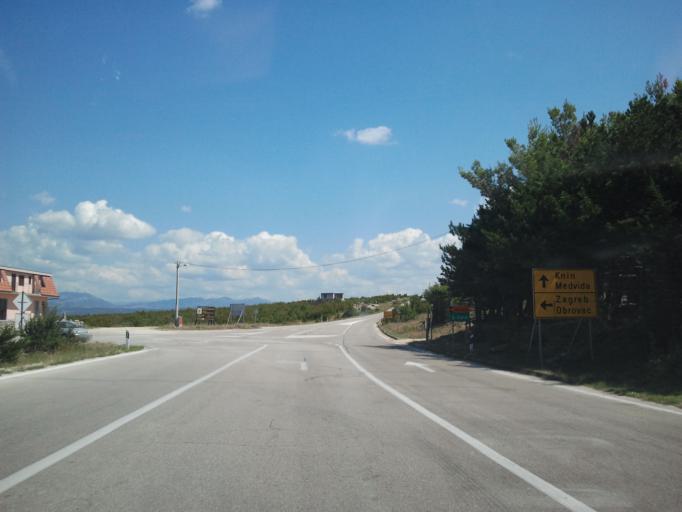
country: HR
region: Zadarska
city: Obrovac
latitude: 44.1945
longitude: 15.6812
